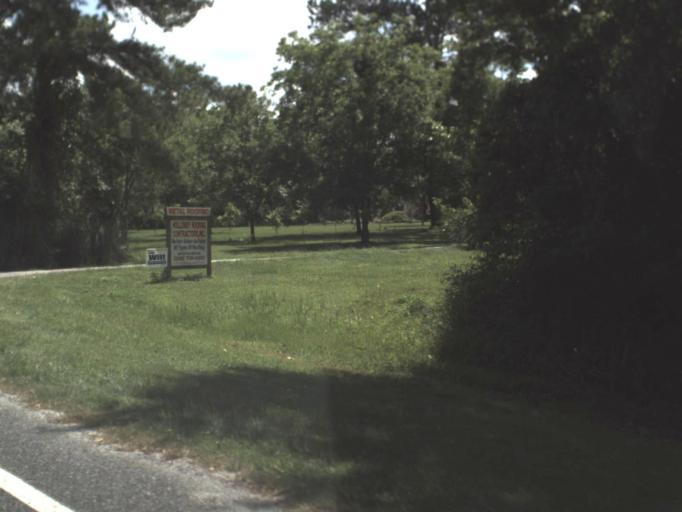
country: US
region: Florida
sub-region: Alachua County
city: High Springs
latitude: 29.9785
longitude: -82.5991
